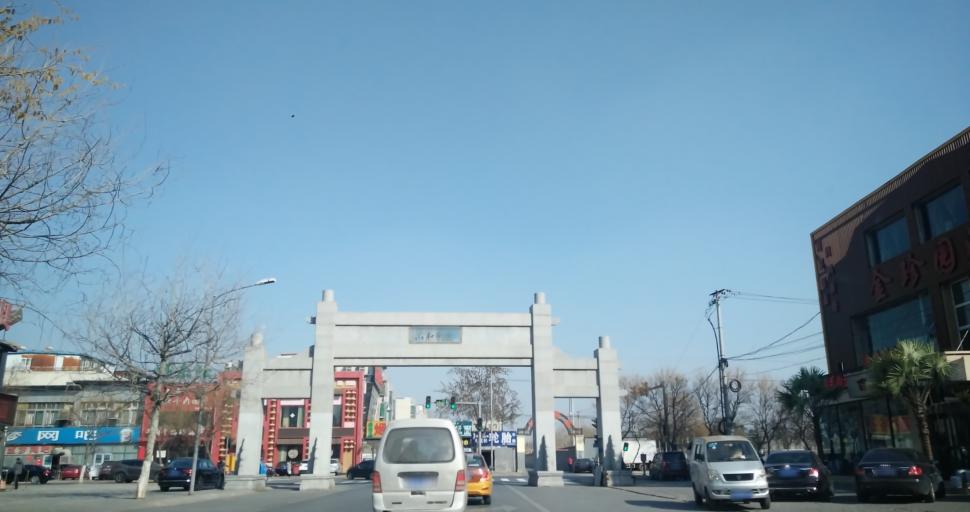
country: CN
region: Beijing
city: Jiugong
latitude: 39.8085
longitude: 116.4490
